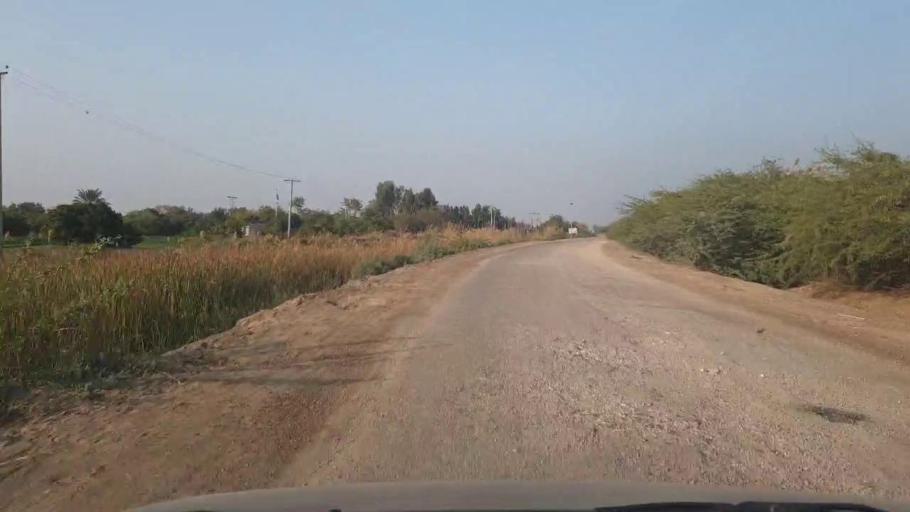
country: PK
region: Sindh
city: Mirwah Gorchani
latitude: 25.3261
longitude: 69.1651
